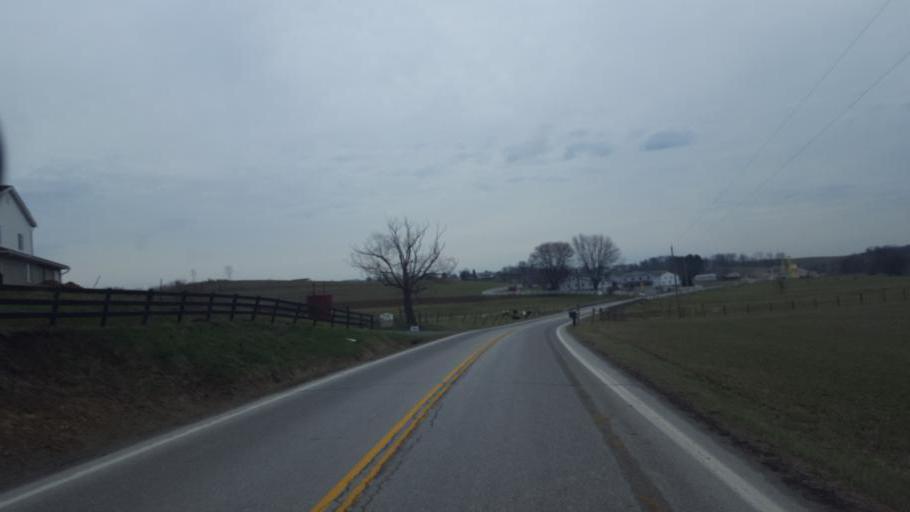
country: US
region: Ohio
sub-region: Tuscarawas County
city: Sugarcreek
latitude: 40.4858
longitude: -81.7432
